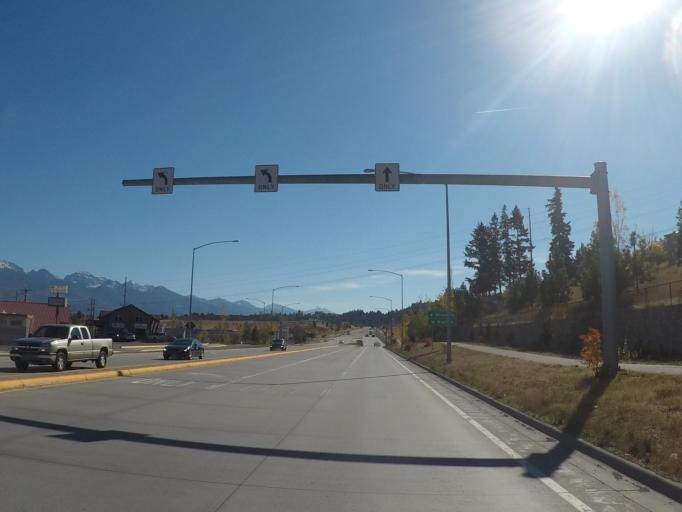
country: US
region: Montana
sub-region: Lake County
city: Polson
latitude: 47.6904
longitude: -114.1268
